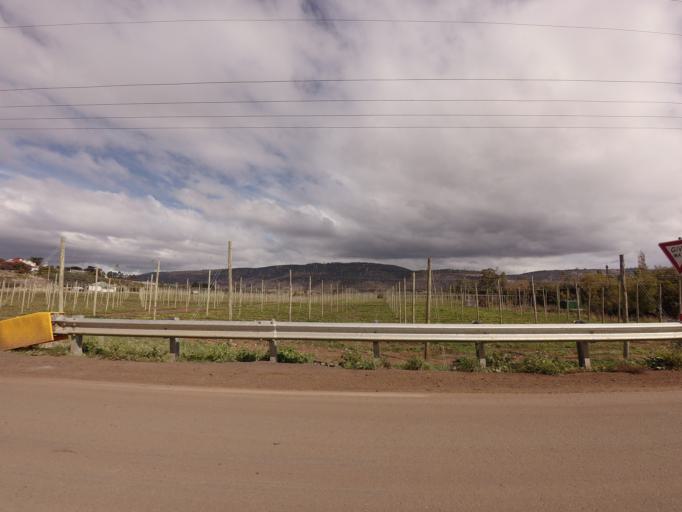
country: AU
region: Tasmania
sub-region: Derwent Valley
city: New Norfolk
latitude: -42.7088
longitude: 146.9105
